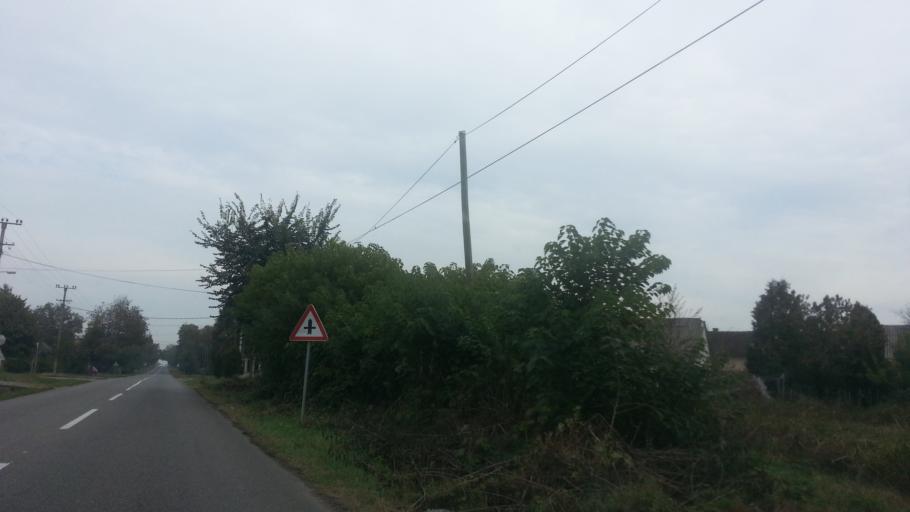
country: RS
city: Belegis
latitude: 45.0225
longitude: 20.3356
